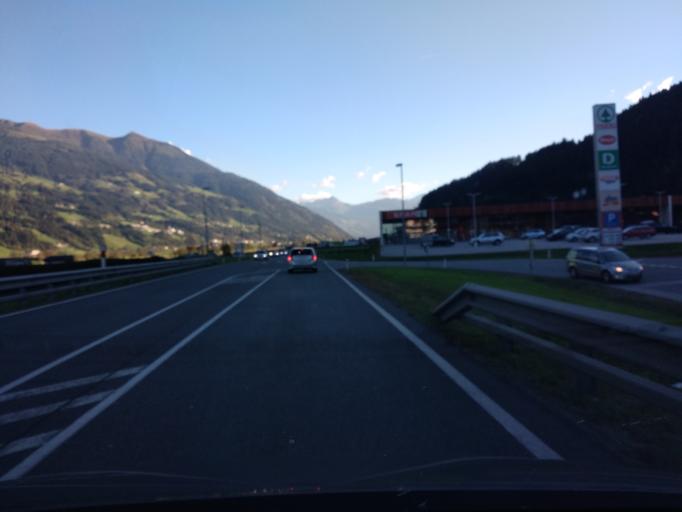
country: AT
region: Tyrol
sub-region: Politischer Bezirk Schwaz
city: Schlitters
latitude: 47.3756
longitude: 11.8442
